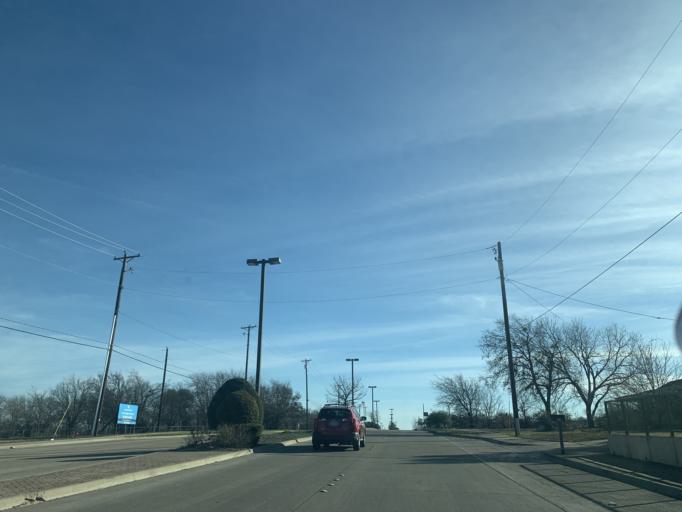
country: US
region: Texas
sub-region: Dallas County
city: DeSoto
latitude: 32.5750
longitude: -96.8392
